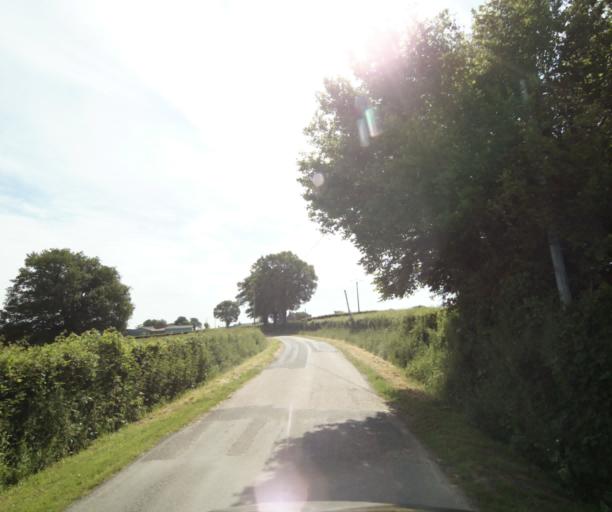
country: FR
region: Bourgogne
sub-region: Departement de Saone-et-Loire
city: Palinges
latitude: 46.5415
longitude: 4.1564
